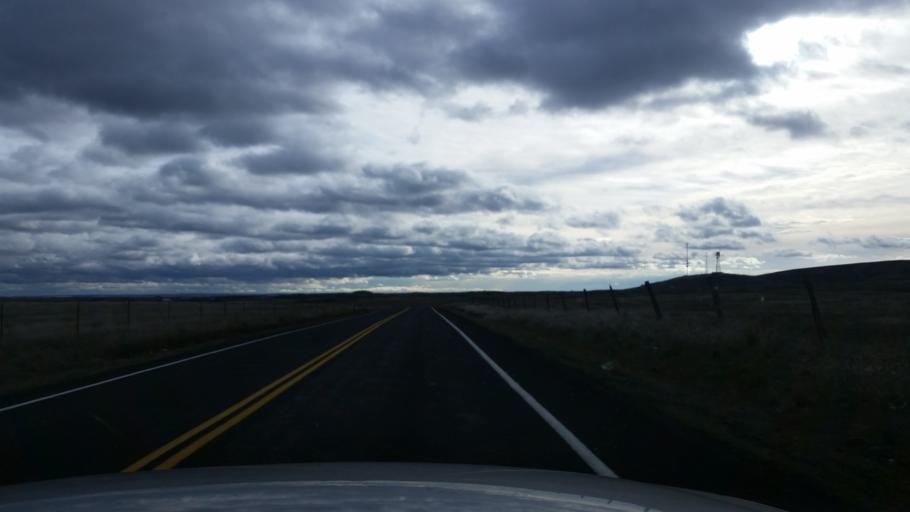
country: US
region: Washington
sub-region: Lincoln County
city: Davenport
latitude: 47.3308
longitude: -117.9833
